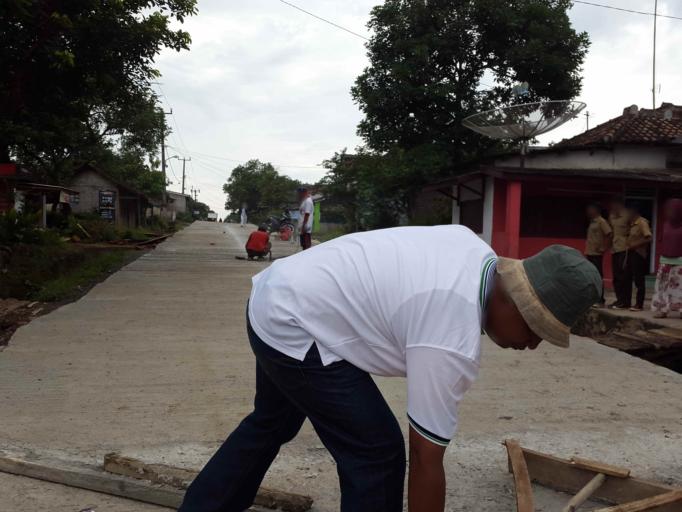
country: ID
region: Lampung
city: Sidorejo
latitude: -5.5326
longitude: 105.4264
